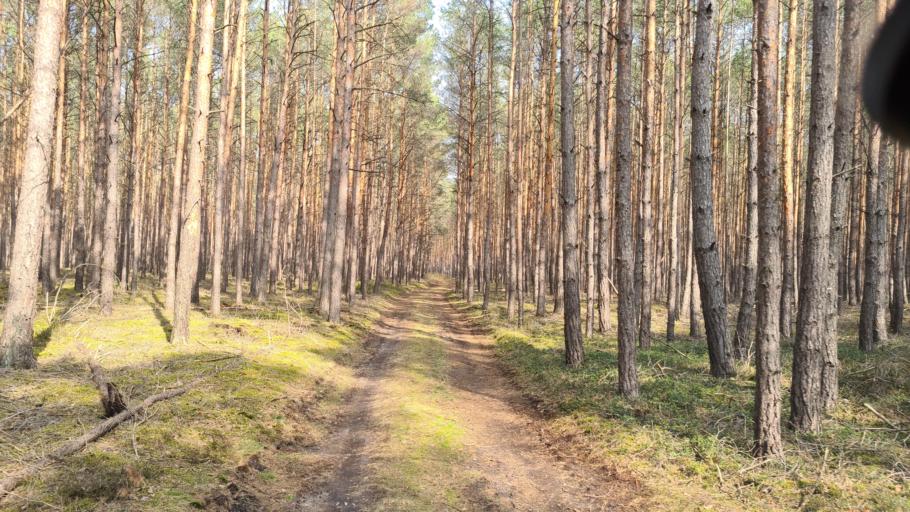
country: DE
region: Brandenburg
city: Schonborn
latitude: 51.6570
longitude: 13.4628
